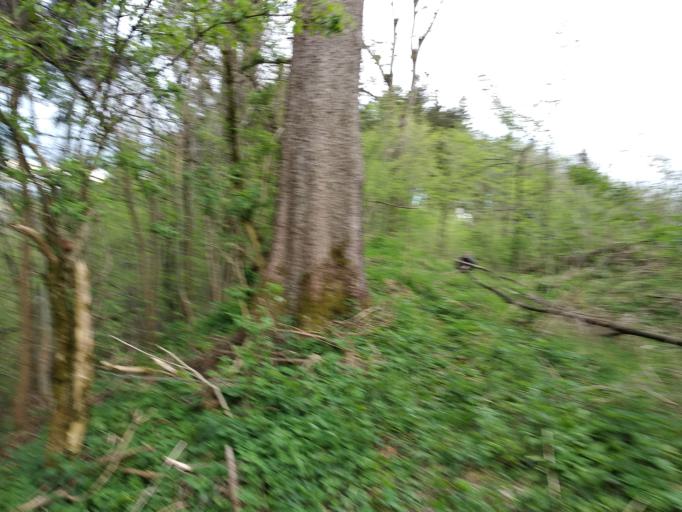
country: DE
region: Bavaria
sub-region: Swabia
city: Kronburg
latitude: 47.8966
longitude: 10.1702
